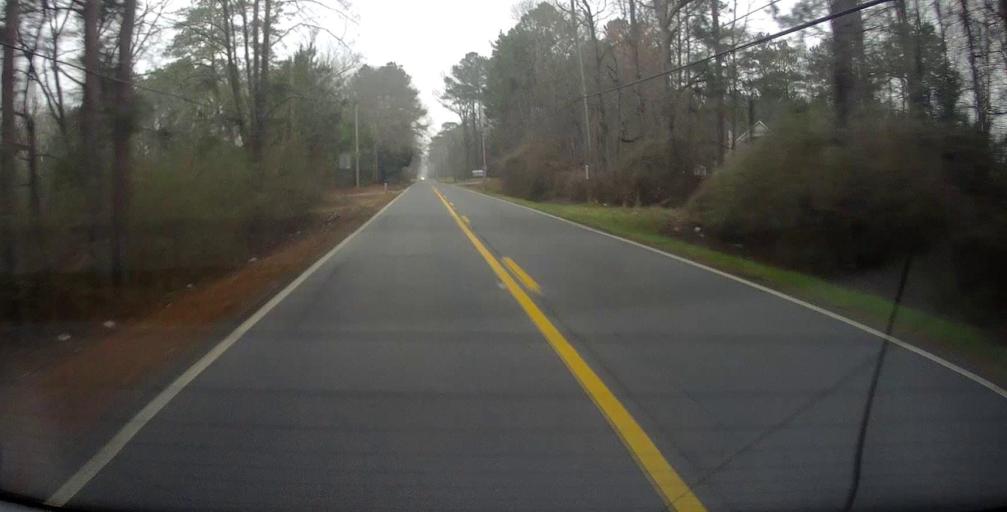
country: US
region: Georgia
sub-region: Spalding County
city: East Griffin
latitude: 33.2130
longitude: -84.2330
